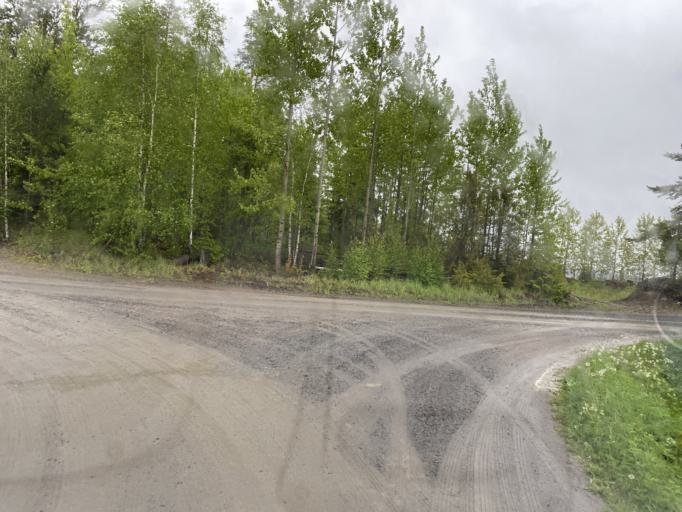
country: FI
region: Haeme
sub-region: Forssa
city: Forssa
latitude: 60.9565
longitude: 23.6017
